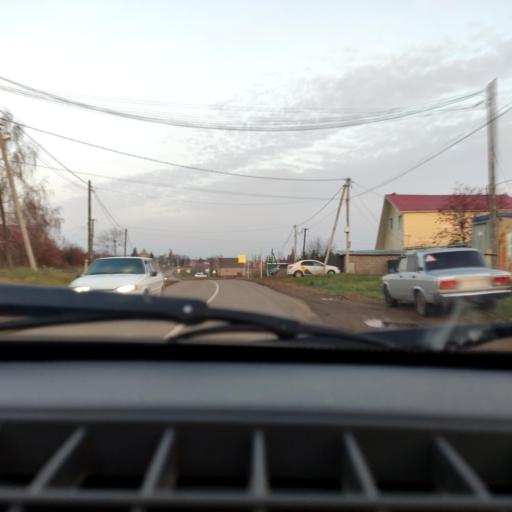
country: RU
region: Bashkortostan
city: Avdon
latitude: 54.6543
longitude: 55.7702
